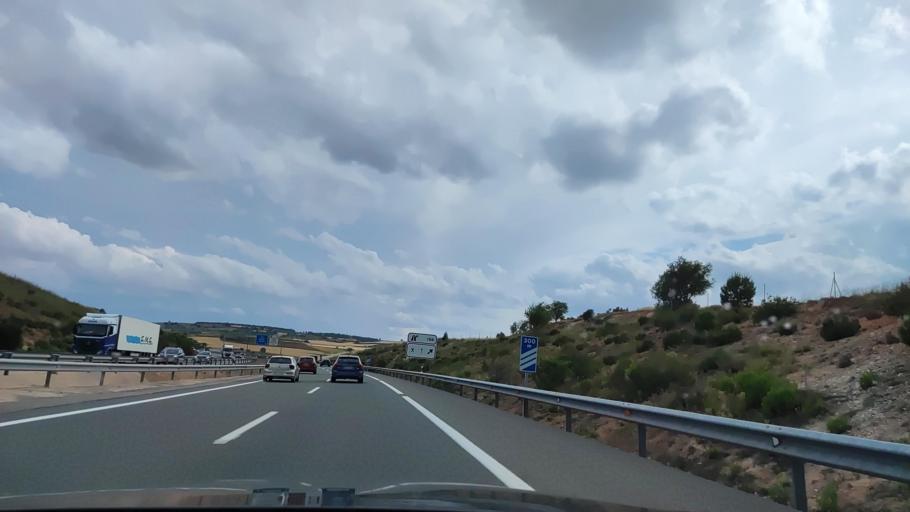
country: ES
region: Castille-La Mancha
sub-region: Provincia de Cuenca
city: Castillo de Garcimunoz
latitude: 39.6936
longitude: -2.3915
